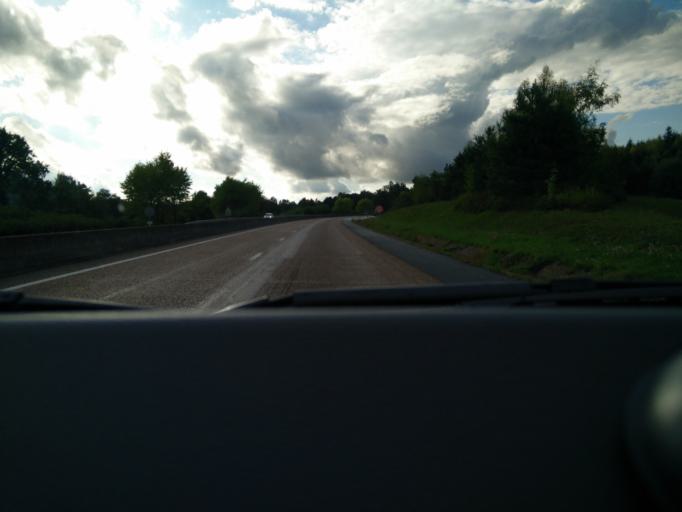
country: FR
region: Lorraine
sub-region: Departement de Meurthe-et-Moselle
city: Baccarat
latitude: 48.4380
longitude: 6.7702
